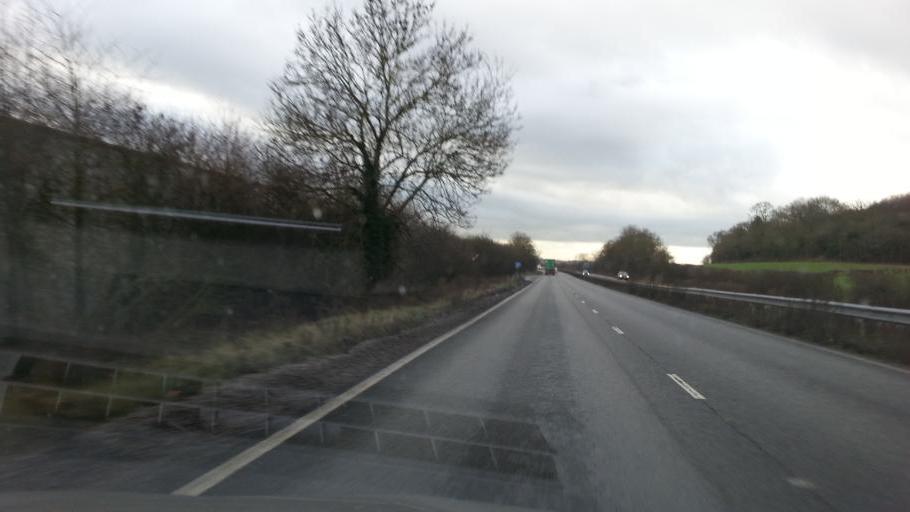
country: GB
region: England
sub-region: Staffordshire
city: Burton upon Trent
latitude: 52.8068
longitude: -1.6642
